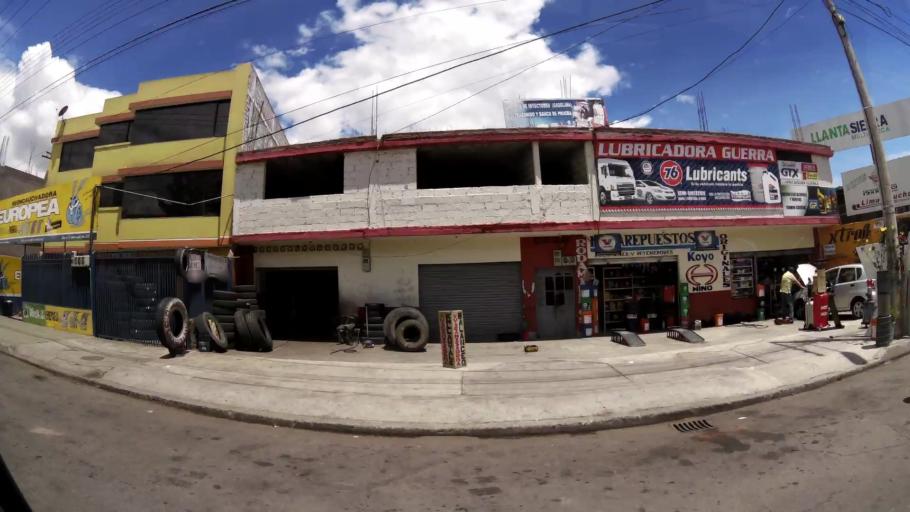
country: EC
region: Tungurahua
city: Ambato
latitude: -1.2638
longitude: -78.6126
